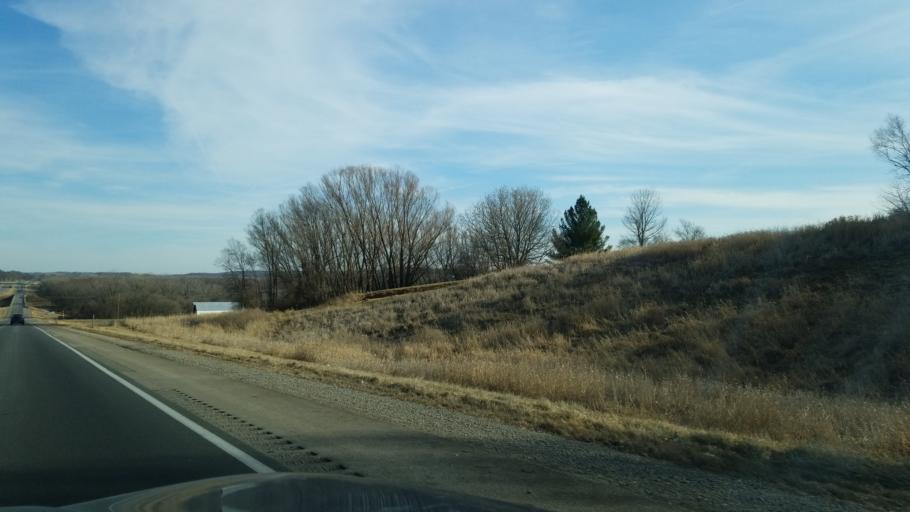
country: US
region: Iowa
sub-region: Linn County
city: Ely
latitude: 41.9255
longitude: -91.5598
